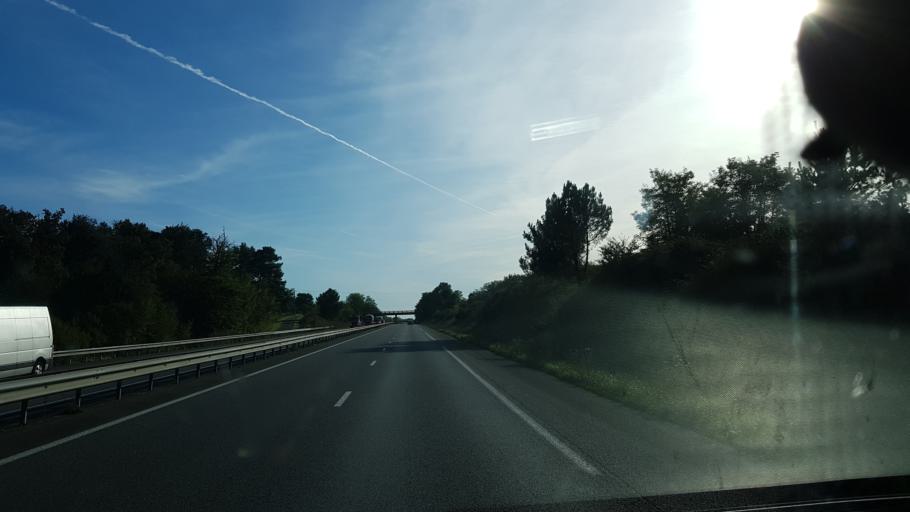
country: FR
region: Poitou-Charentes
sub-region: Departement de la Charente-Maritime
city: Chevanceaux
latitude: 45.2801
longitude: -0.2436
